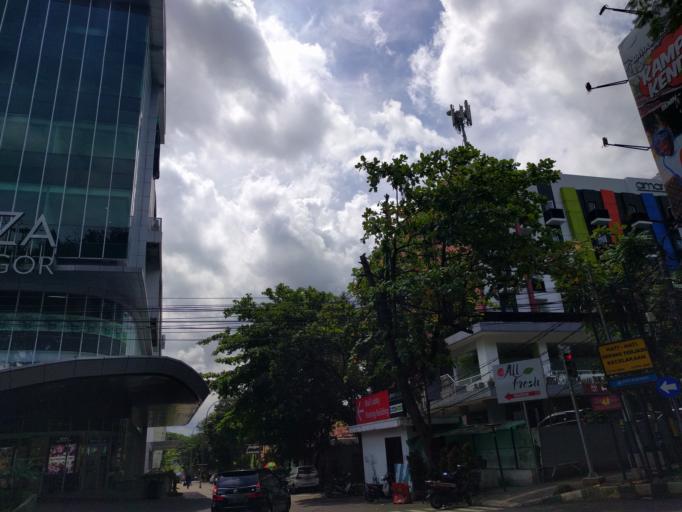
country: ID
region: West Java
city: Bogor
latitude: -6.5958
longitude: 106.8043
